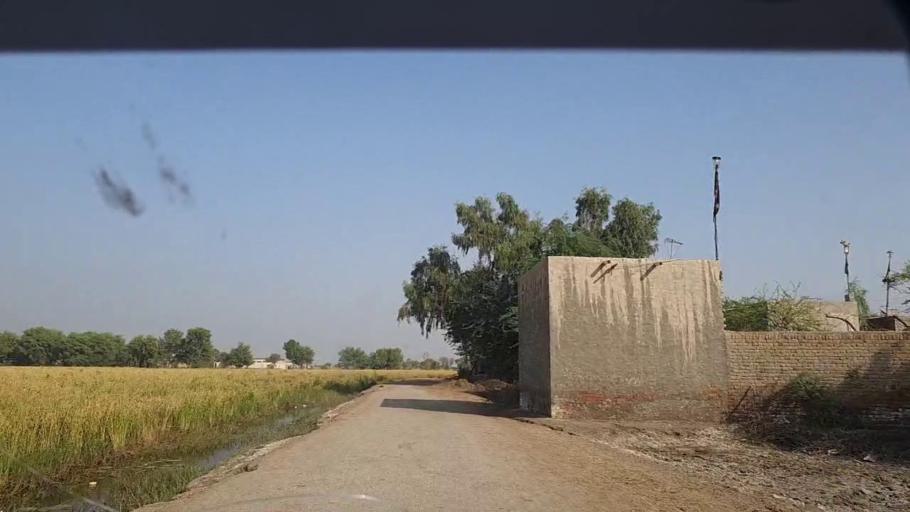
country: PK
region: Sindh
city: Shikarpur
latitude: 28.1170
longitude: 68.5796
